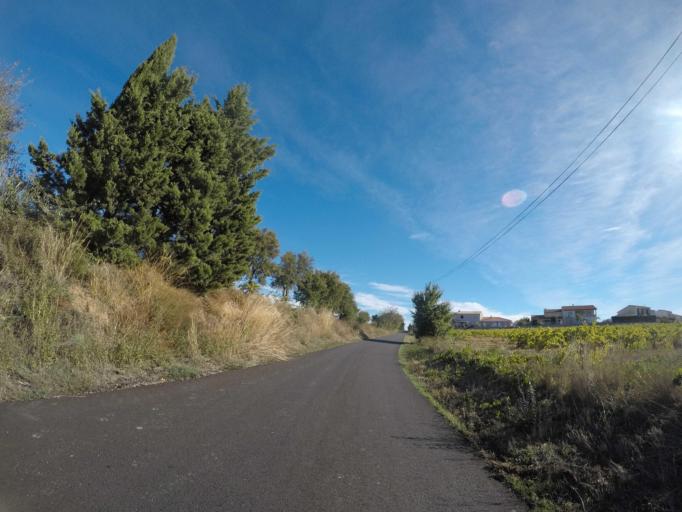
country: FR
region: Languedoc-Roussillon
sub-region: Departement des Pyrenees-Orientales
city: Villemolaque
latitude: 42.5764
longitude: 2.8068
